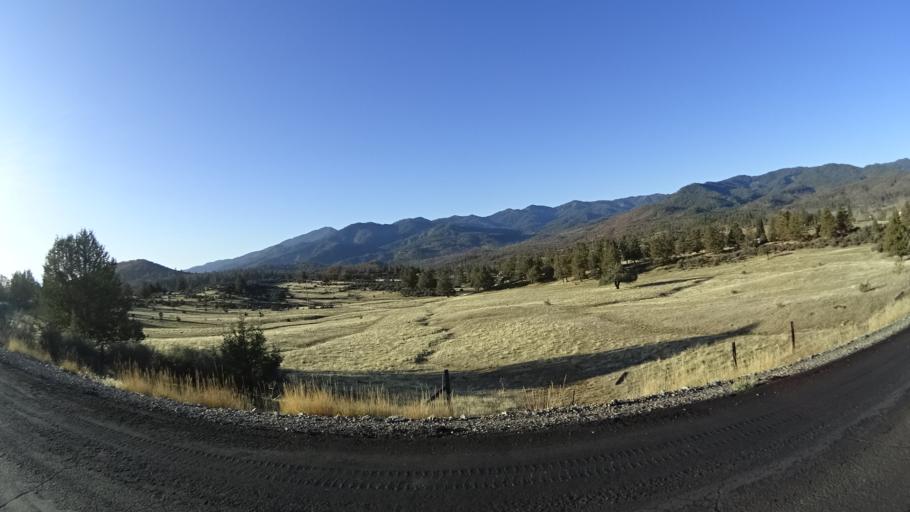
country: US
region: Oregon
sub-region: Jackson County
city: Ashland
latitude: 41.9958
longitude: -122.6165
